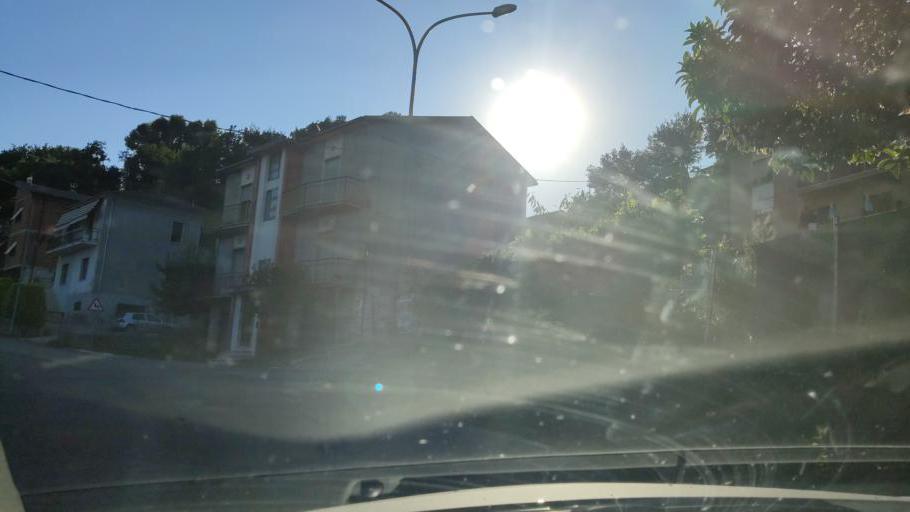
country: IT
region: Umbria
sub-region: Provincia di Terni
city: Narni Scalo
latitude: 42.5398
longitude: 12.5181
